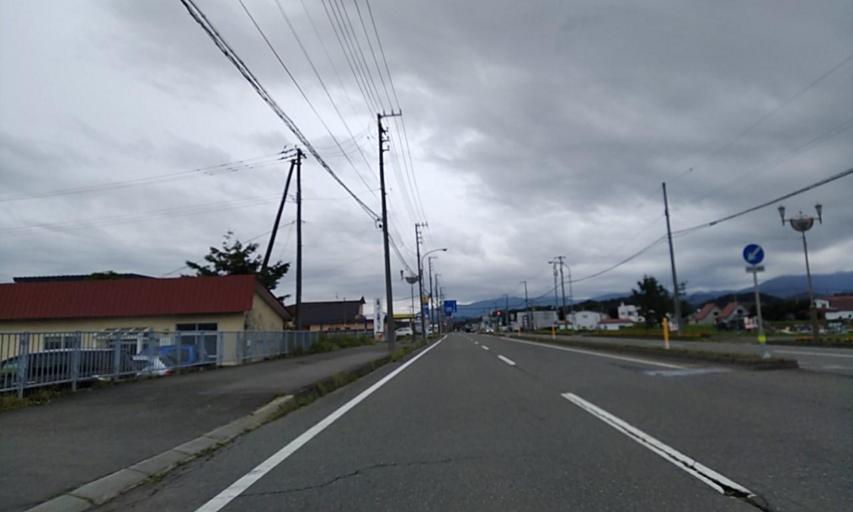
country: JP
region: Hokkaido
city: Obihiro
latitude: 42.3044
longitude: 143.3177
